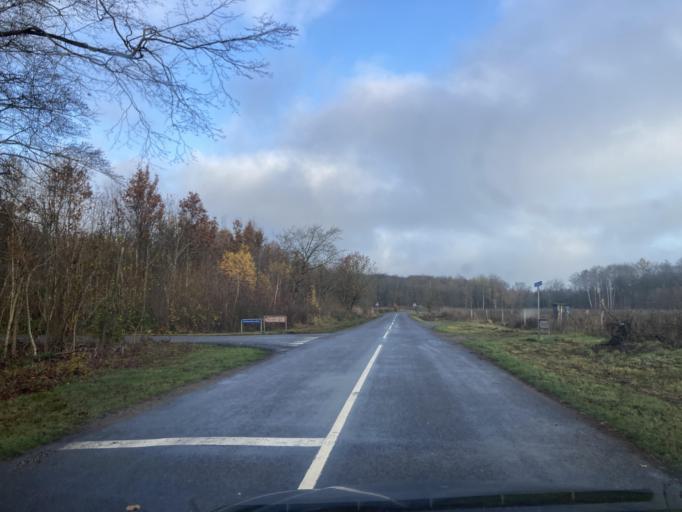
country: DK
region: Zealand
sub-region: Lolland Kommune
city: Rodby
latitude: 54.7846
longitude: 11.3742
